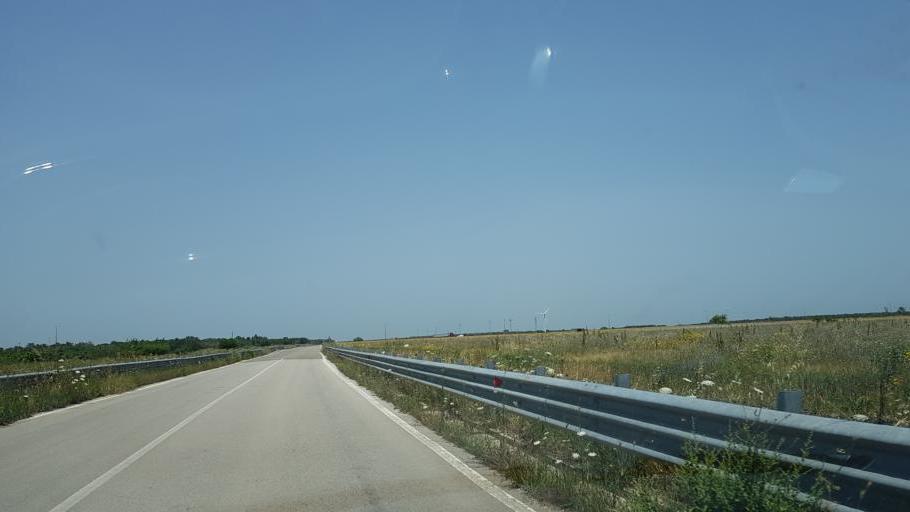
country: IT
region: Apulia
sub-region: Provincia di Brindisi
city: Mesagne
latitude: 40.4973
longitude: 17.8293
